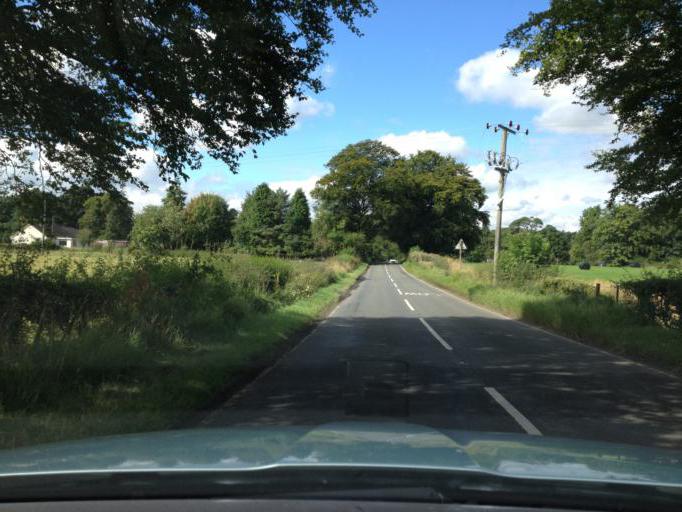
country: GB
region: Scotland
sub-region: West Lothian
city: Armadale
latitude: 55.9227
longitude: -3.6894
